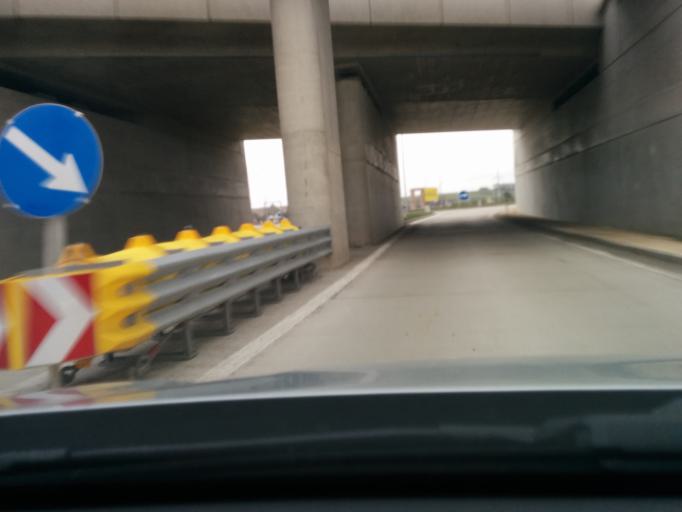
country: AT
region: Lower Austria
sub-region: Politischer Bezirk Mistelbach
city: Mistelbach
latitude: 48.5626
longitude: 16.5546
